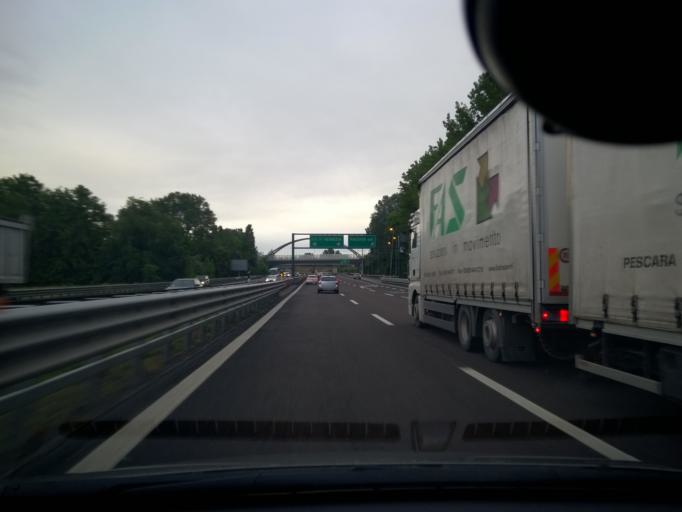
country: IT
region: Veneto
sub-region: Provincia di Padova
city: Noventa
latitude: 45.4219
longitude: 11.9328
